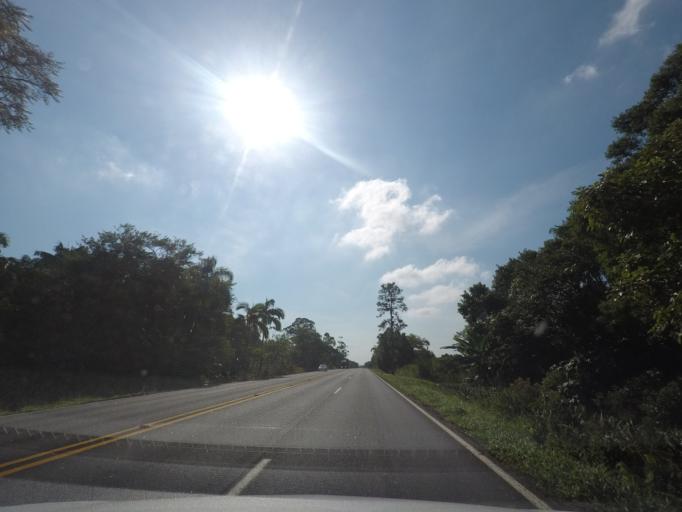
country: BR
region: Parana
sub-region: Pontal Do Parana
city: Pontal do Parana
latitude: -25.6400
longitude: -48.5916
